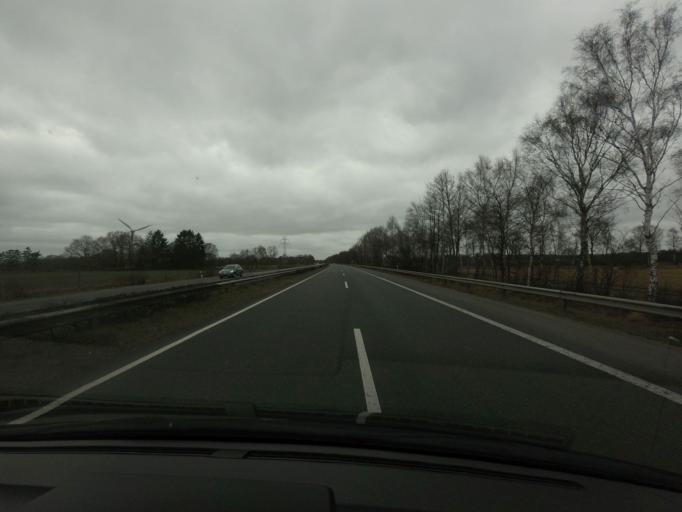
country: DE
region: Lower Saxony
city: Wiefelstede
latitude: 53.1996
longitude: 8.0910
